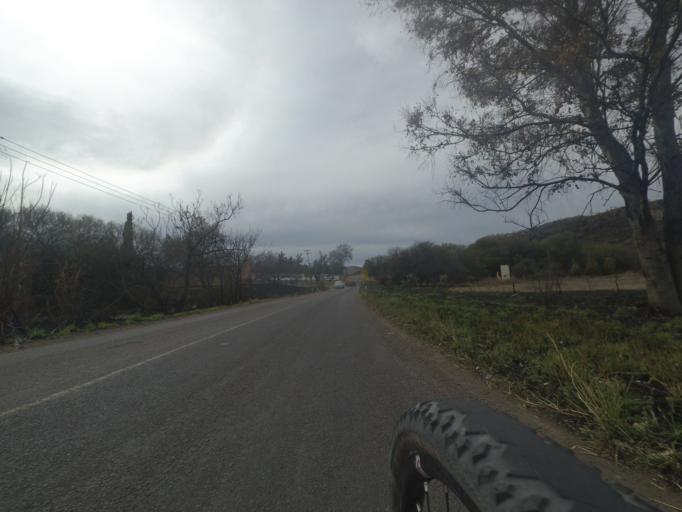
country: MX
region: Aguascalientes
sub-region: Aguascalientes
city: La Loma de los Negritos
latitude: 21.8356
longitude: -102.3685
